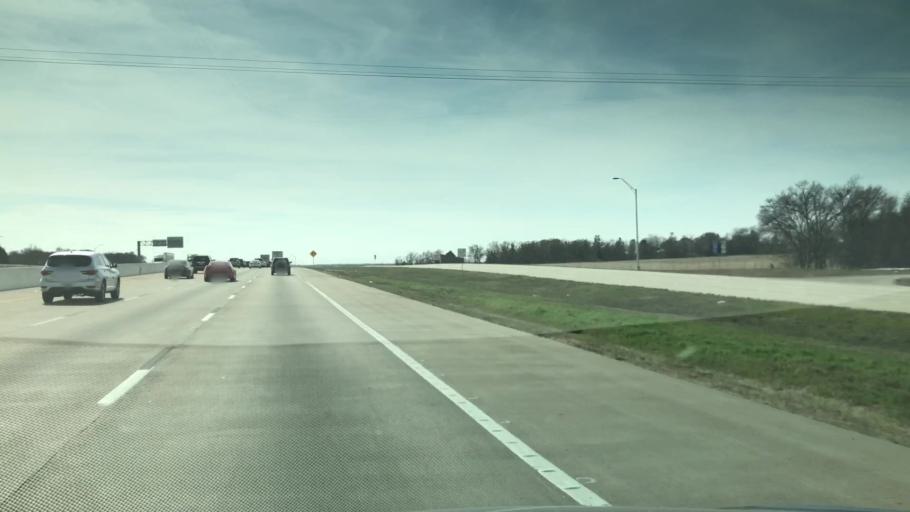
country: US
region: Texas
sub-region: McLennan County
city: West
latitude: 31.8285
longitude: -97.0943
